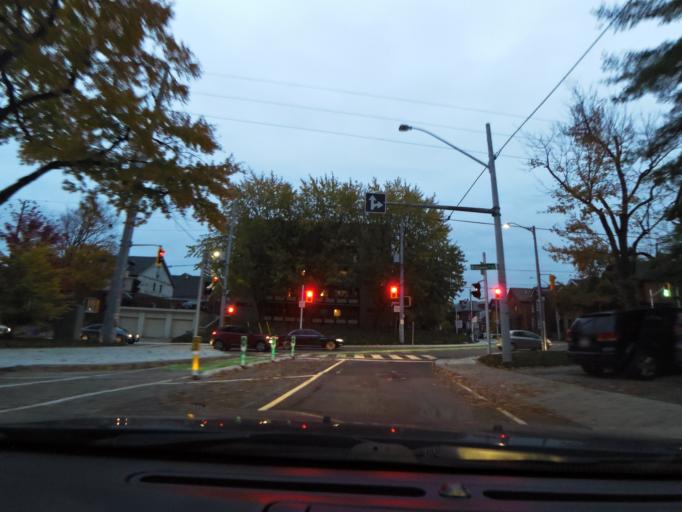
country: CA
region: Ontario
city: Hamilton
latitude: 43.2514
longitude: -79.8823
